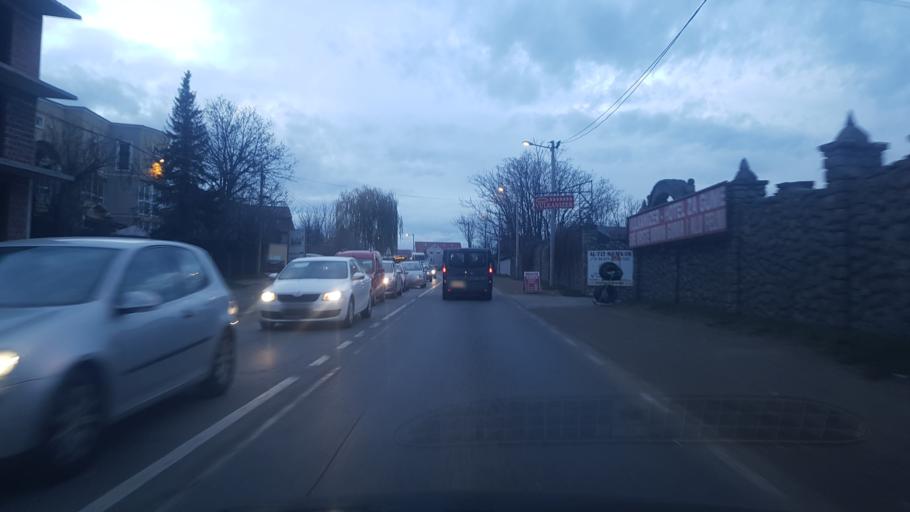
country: RS
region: Central Serbia
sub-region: Belgrade
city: Zemun
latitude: 44.8078
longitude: 20.3591
